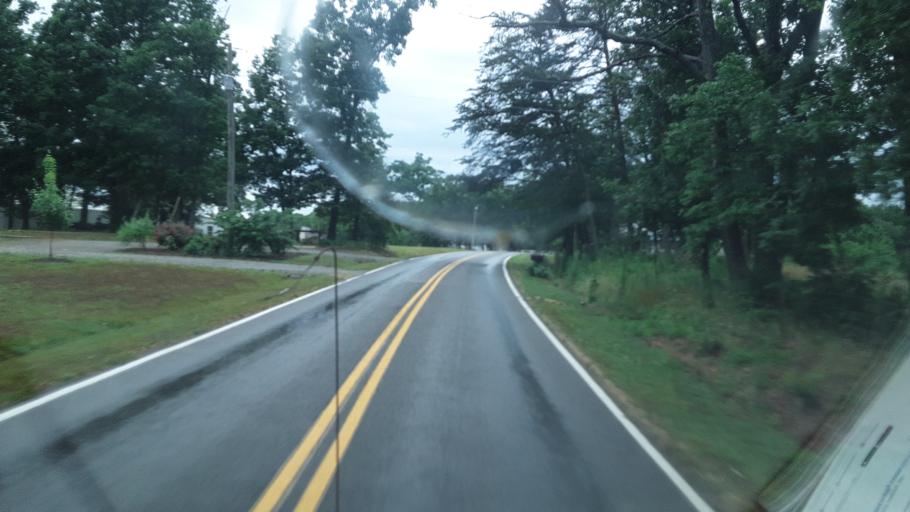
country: US
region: North Carolina
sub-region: Yadkin County
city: Jonesville
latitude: 36.0847
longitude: -80.8589
